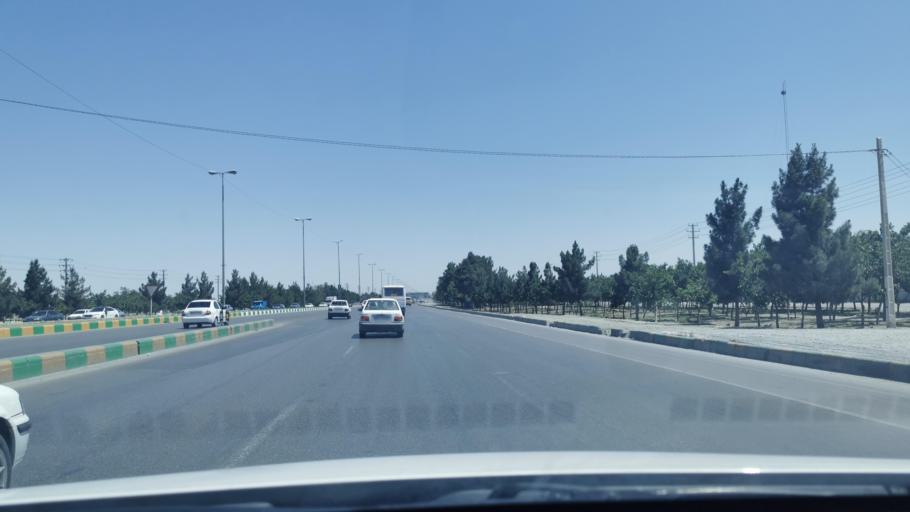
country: IR
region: Razavi Khorasan
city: Torqabeh
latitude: 36.4185
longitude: 59.4644
